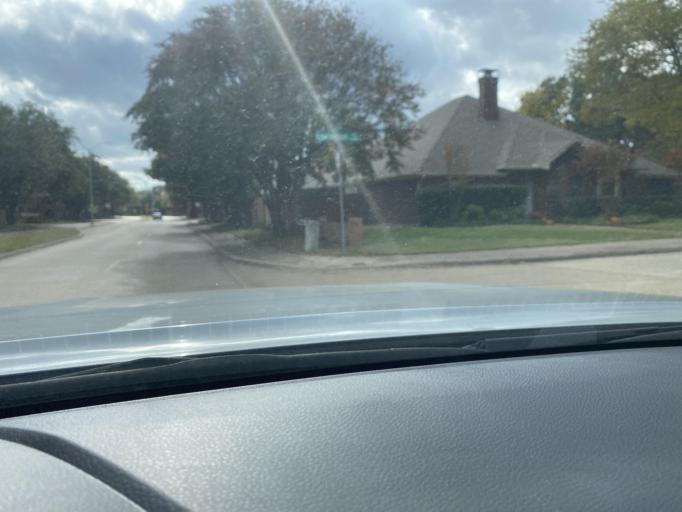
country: US
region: Texas
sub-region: Dallas County
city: Addison
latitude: 33.0032
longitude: -96.7845
